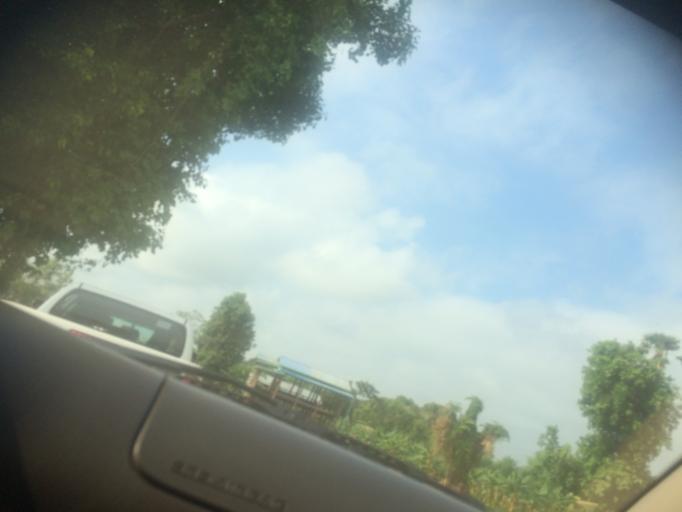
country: MM
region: Bago
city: Pyay
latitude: 18.6696
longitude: 95.0537
